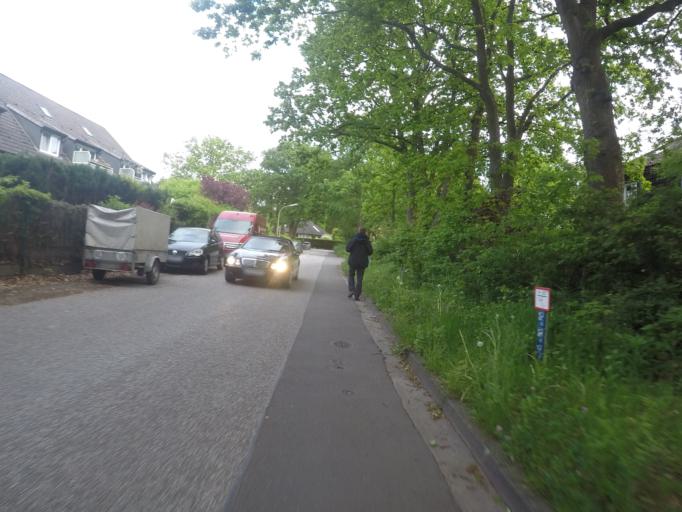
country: DE
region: Schleswig-Holstein
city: Bonningstedt
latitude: 53.6510
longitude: 9.9257
